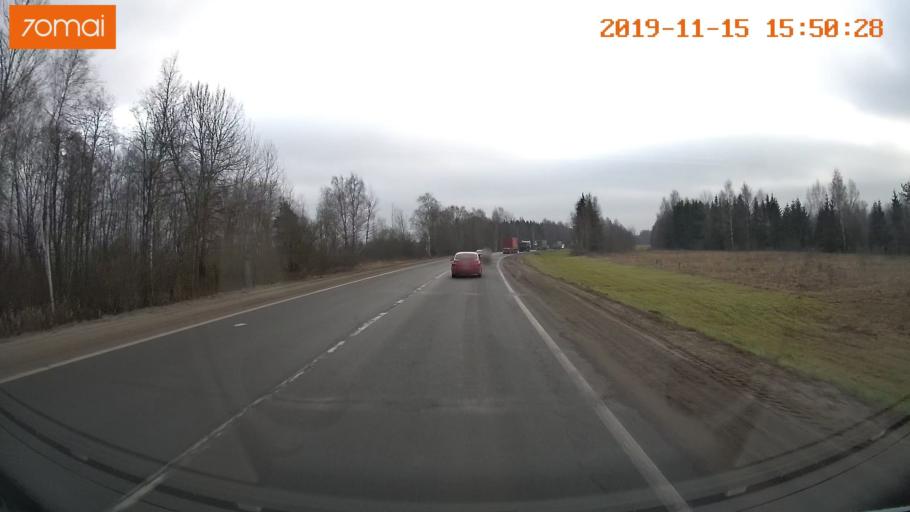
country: RU
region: Jaroslavl
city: Yaroslavl
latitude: 57.9051
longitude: 40.0134
